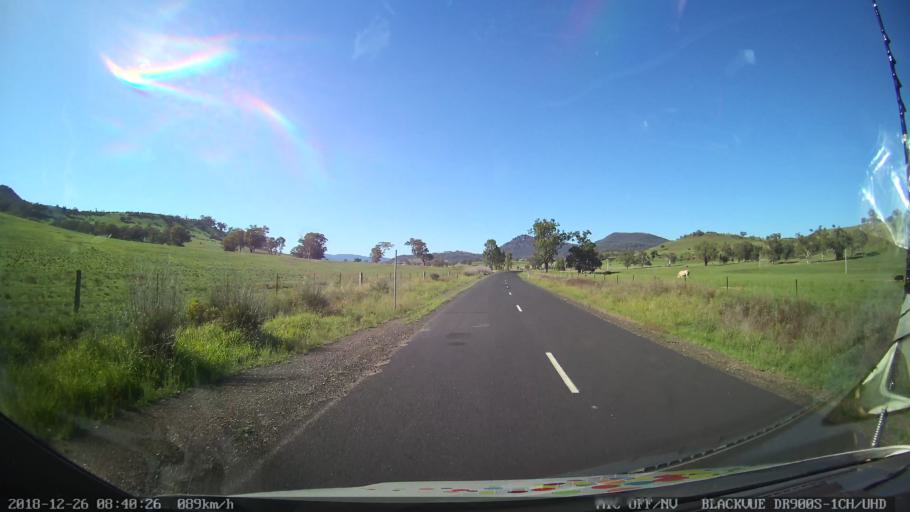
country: AU
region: New South Wales
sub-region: Mid-Western Regional
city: Kandos
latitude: -32.4667
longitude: 150.0762
